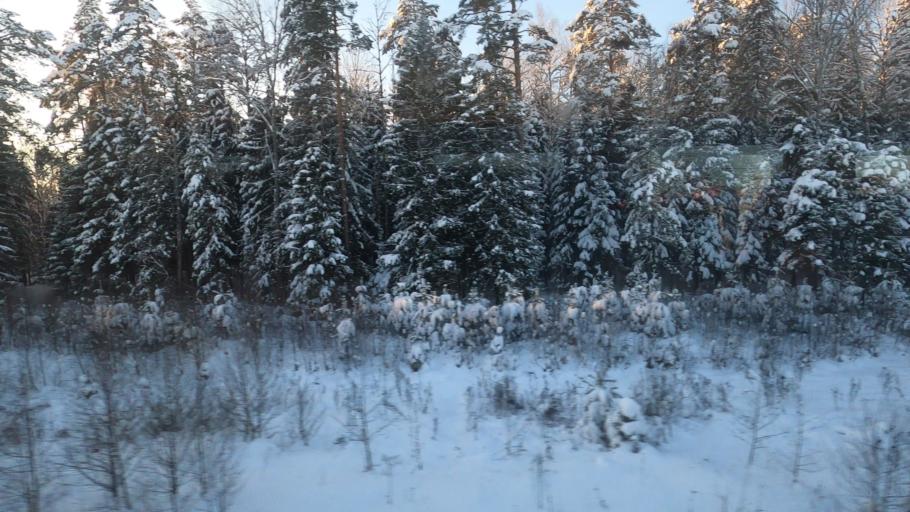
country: RU
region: Moskovskaya
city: Verbilki
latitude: 56.5225
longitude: 37.5577
